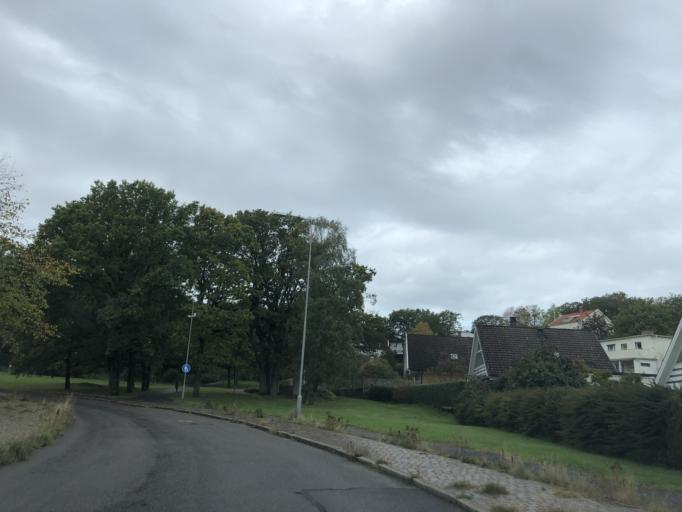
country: SE
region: Vaestra Goetaland
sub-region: Goteborg
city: Majorna
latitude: 57.6646
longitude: 11.8707
